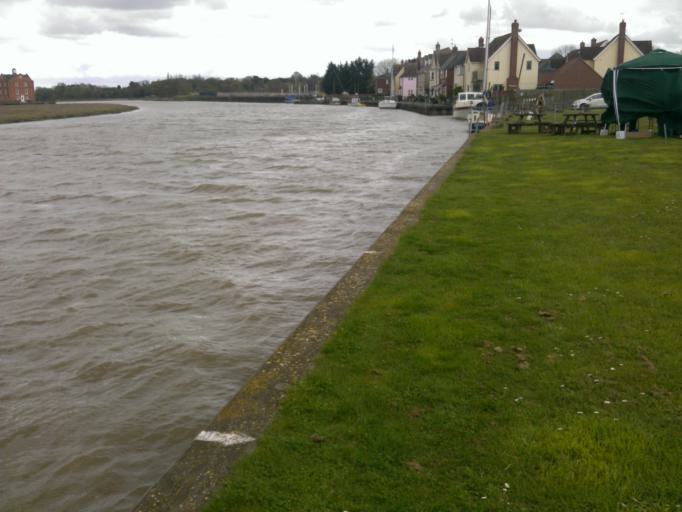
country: GB
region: England
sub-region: Essex
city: Rowhedge
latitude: 51.8561
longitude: 0.9492
